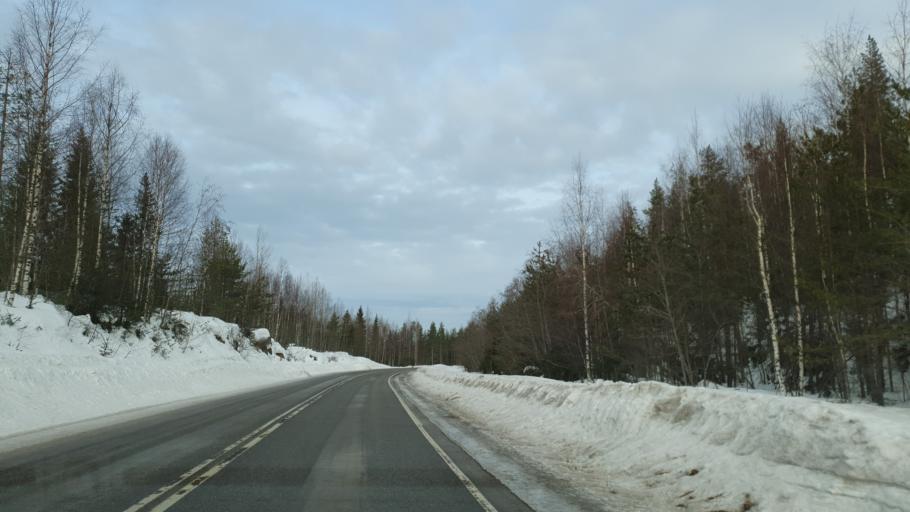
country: FI
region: Kainuu
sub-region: Kajaani
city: Paltamo
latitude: 64.2541
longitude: 28.0350
